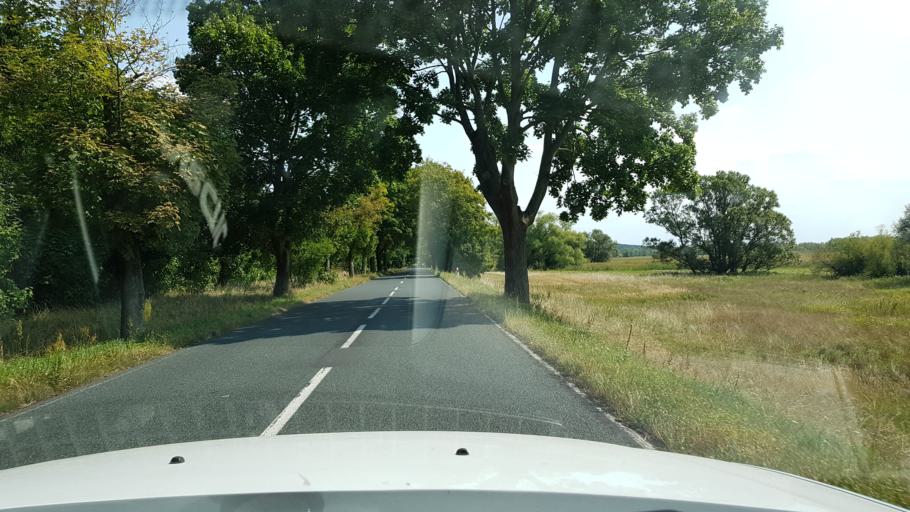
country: PL
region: West Pomeranian Voivodeship
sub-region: Powiat gryfinski
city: Cedynia
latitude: 52.8308
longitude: 14.2138
